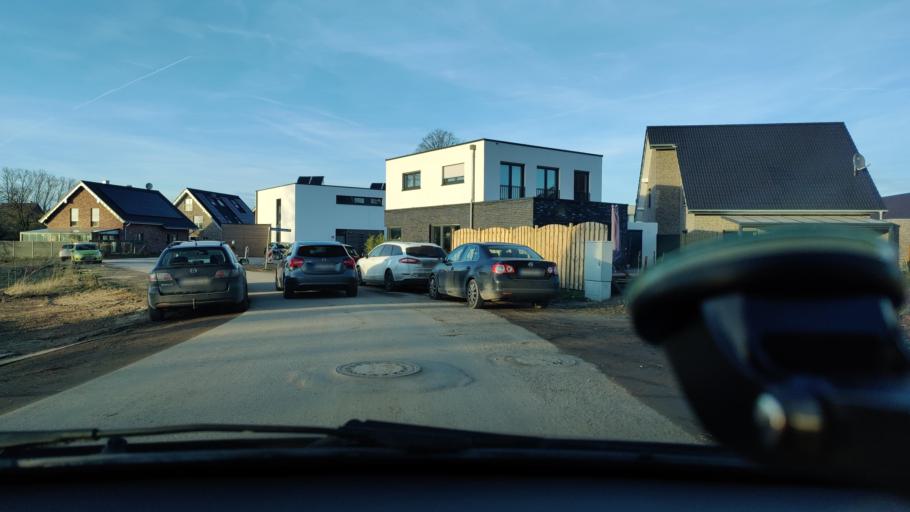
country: DE
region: North Rhine-Westphalia
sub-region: Regierungsbezirk Dusseldorf
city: Goch
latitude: 51.6867
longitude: 6.1639
